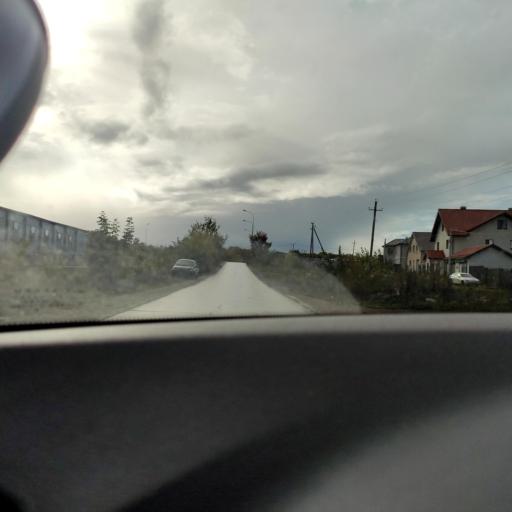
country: RU
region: Samara
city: Novosemeykino
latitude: 53.3827
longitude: 50.3186
